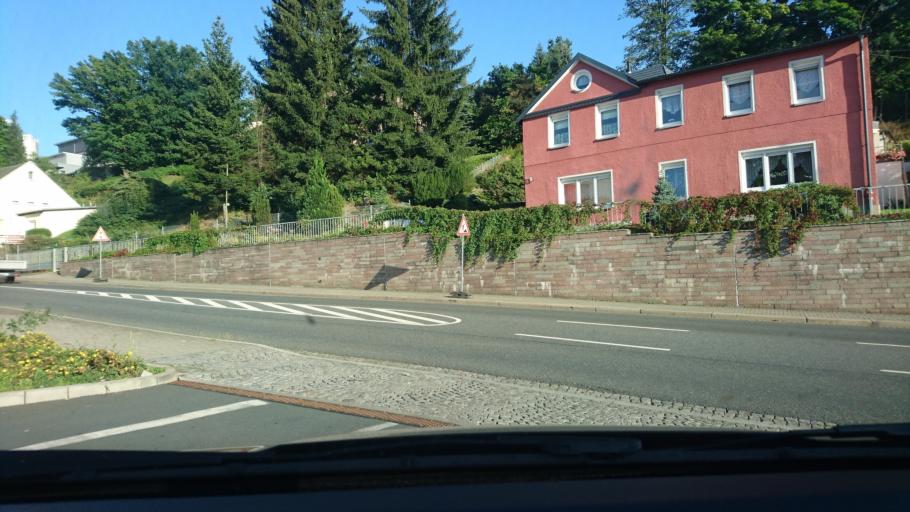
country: DE
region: Saxony
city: Auerbach
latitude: 50.5065
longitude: 12.4019
